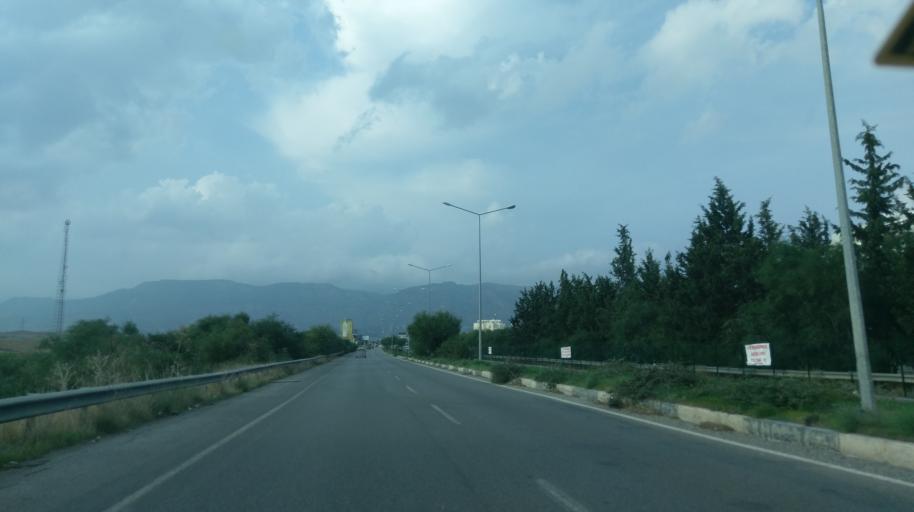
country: CY
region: Keryneia
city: Kyrenia
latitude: 35.2551
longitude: 33.3004
